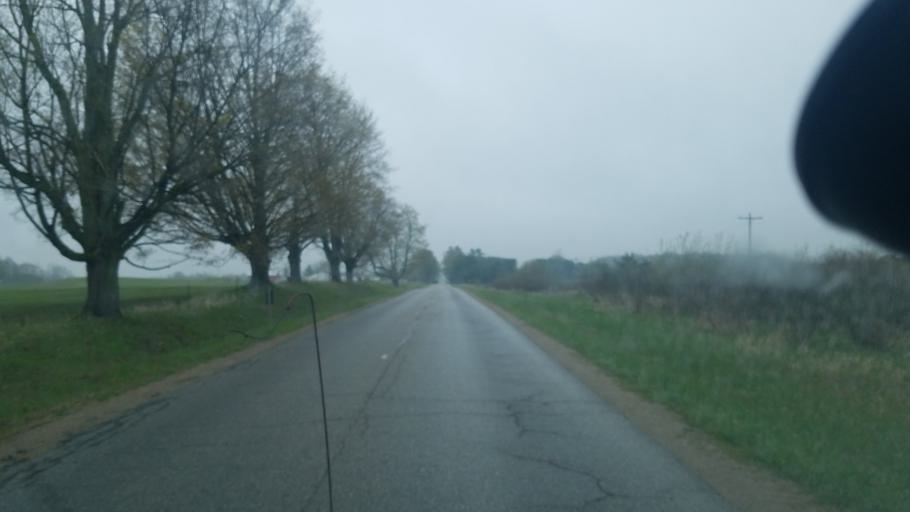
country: US
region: Michigan
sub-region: Montcalm County
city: Lakeview
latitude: 43.5034
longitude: -85.2842
